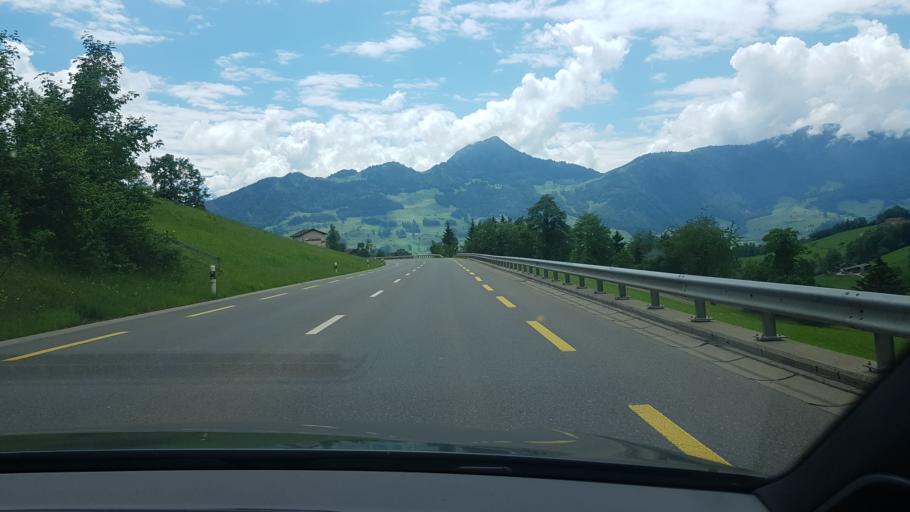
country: CH
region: Schwyz
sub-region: Bezirk Schwyz
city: Steinen
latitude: 47.0649
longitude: 8.6233
